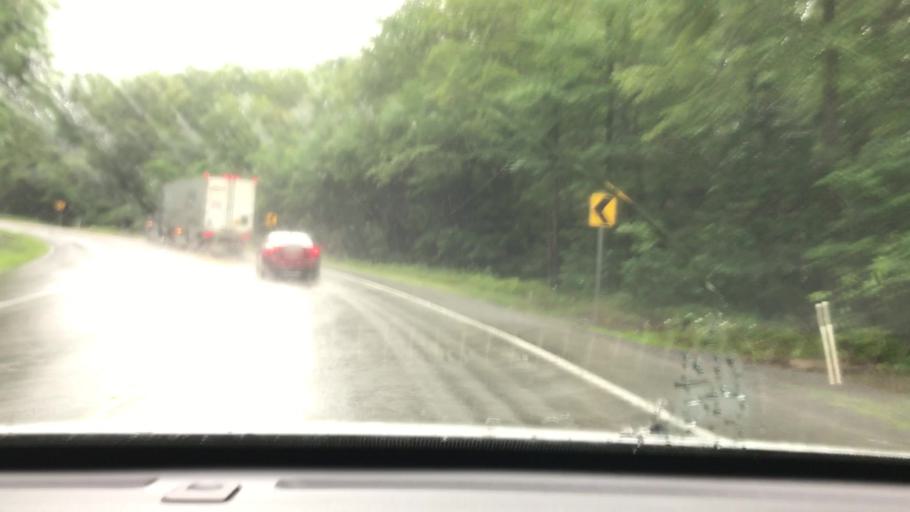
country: US
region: Pennsylvania
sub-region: Clearfield County
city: Osceola Mills
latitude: 40.7739
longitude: -78.2351
